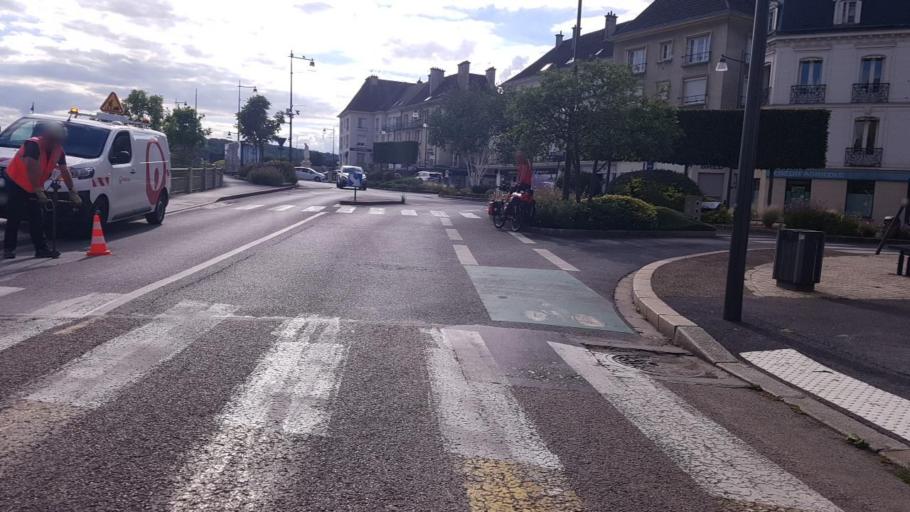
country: FR
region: Picardie
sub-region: Departement de l'Aisne
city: Chateau-Thierry
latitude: 49.0445
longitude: 3.4045
